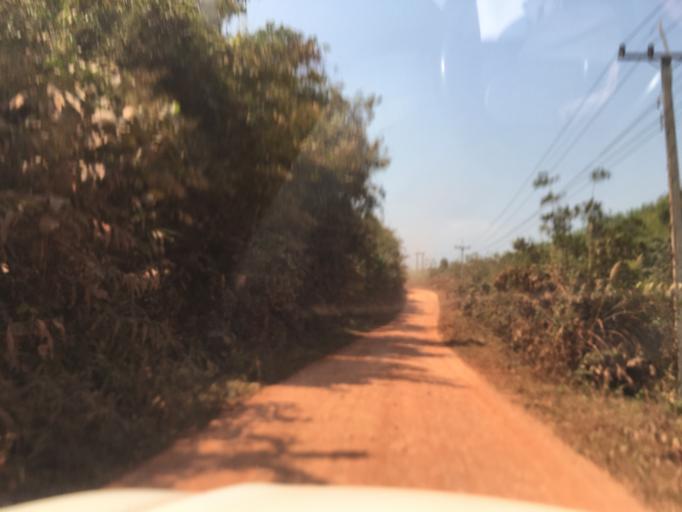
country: LA
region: Bolikhamxai
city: Bolikhan
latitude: 18.7502
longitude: 103.6105
